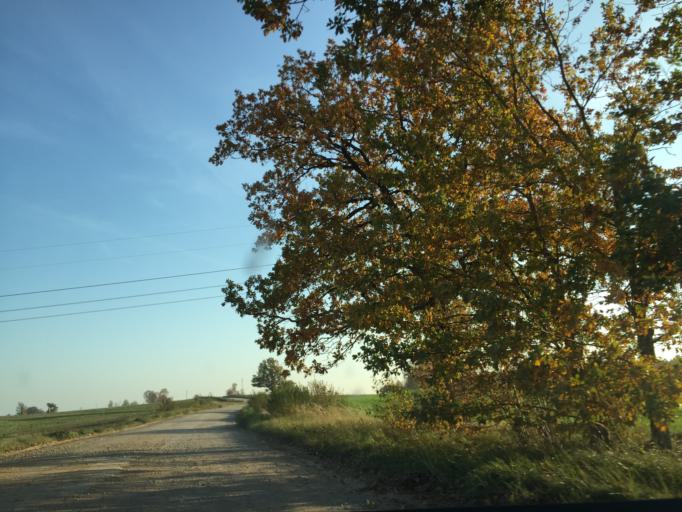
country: LV
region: Vainode
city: Vainode
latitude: 56.6152
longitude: 21.8160
